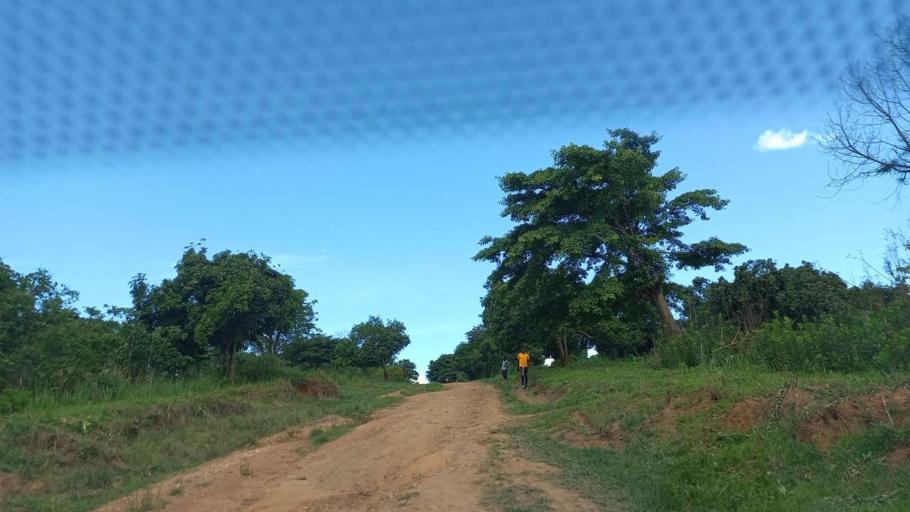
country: ZM
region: North-Western
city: Mwinilunga
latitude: -12.3590
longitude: 24.2327
